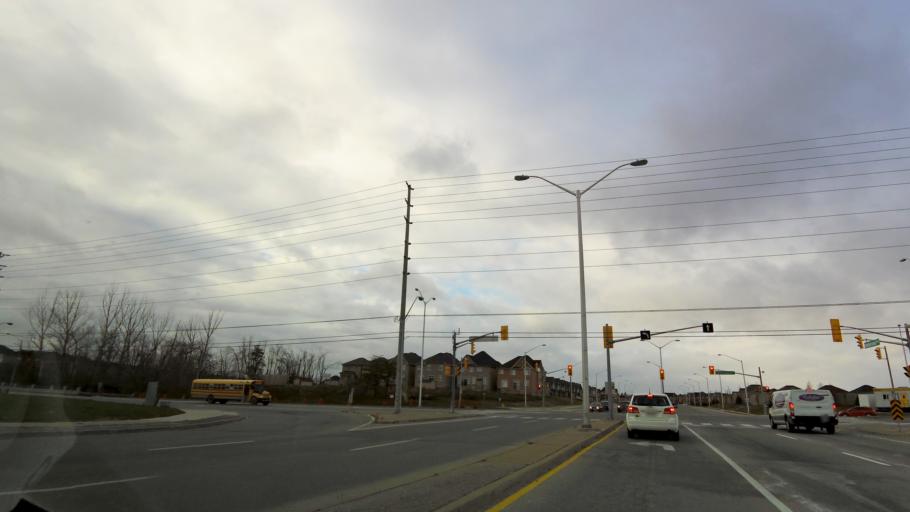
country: CA
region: Ontario
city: Brampton
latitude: 43.7663
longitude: -79.7179
